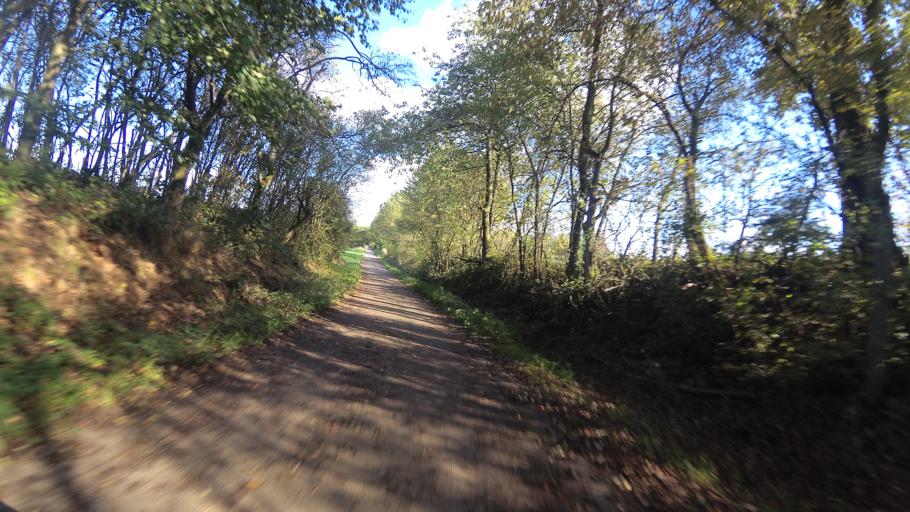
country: DE
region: Saarland
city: Marpingen
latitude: 49.4553
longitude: 7.0335
